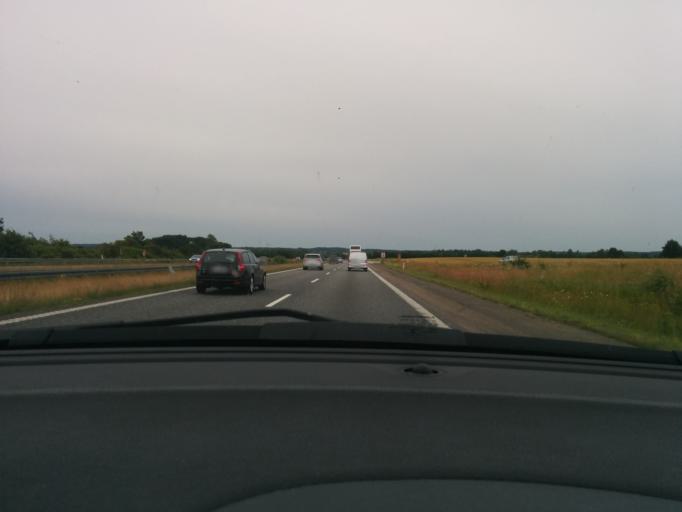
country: DK
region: Zealand
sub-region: Faxe Kommune
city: Ronnede
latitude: 55.2877
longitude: 12.0173
